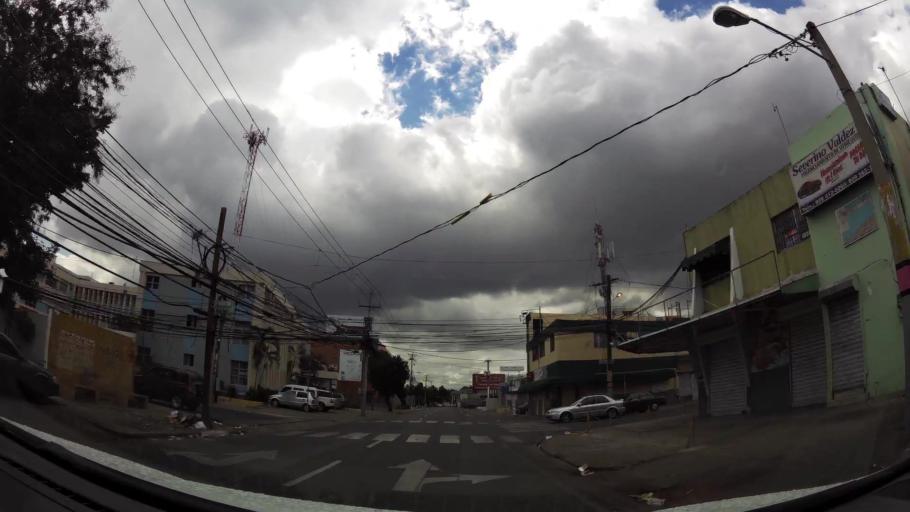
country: DO
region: Nacional
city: San Carlos
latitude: 18.4851
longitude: -69.9185
